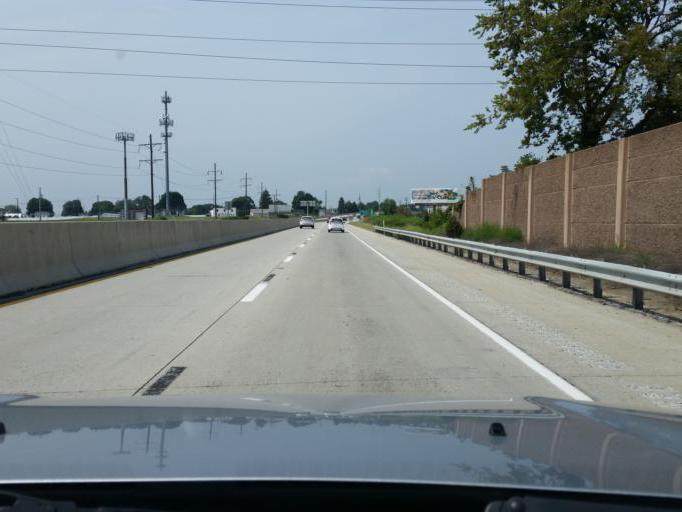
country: US
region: Pennsylvania
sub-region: Cumberland County
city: Shiremanstown
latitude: 40.2340
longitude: -76.9654
